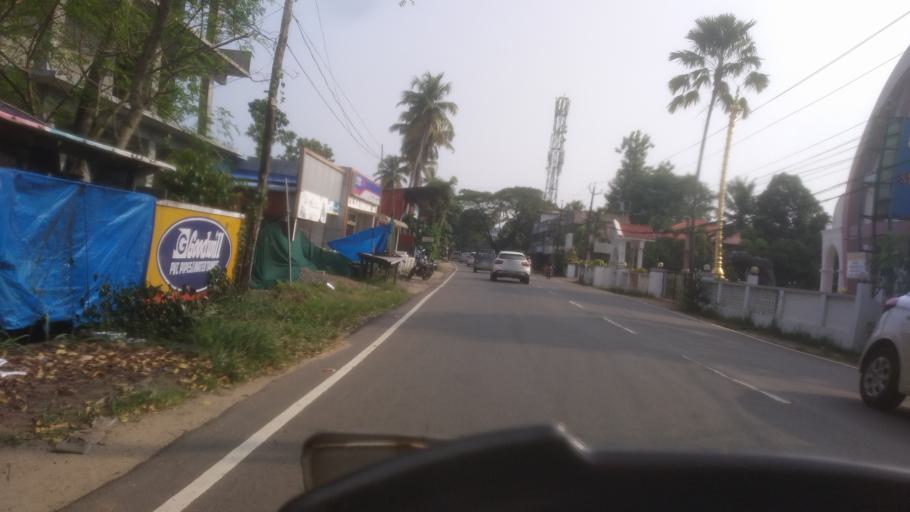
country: IN
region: Kerala
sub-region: Alappuzha
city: Arukutti
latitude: 9.9189
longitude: 76.3622
